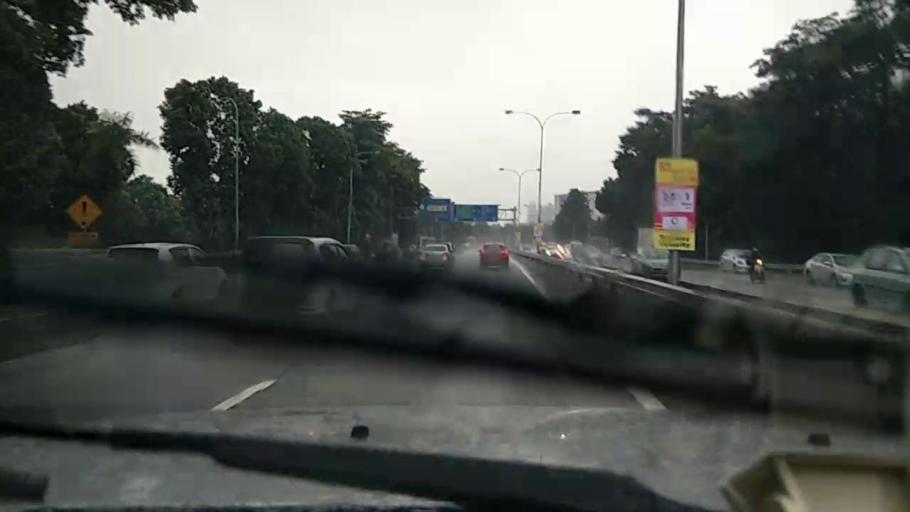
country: MY
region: Kuala Lumpur
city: Kuala Lumpur
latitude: 3.1006
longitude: 101.6985
